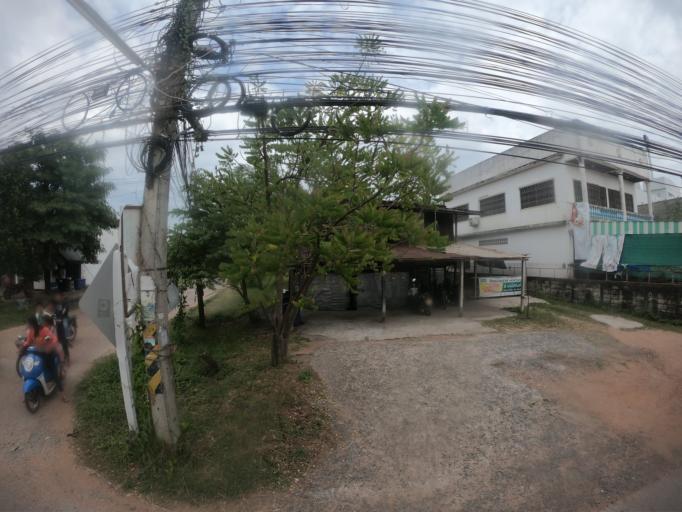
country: TH
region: Maha Sarakham
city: Kantharawichai
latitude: 16.3252
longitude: 103.2980
